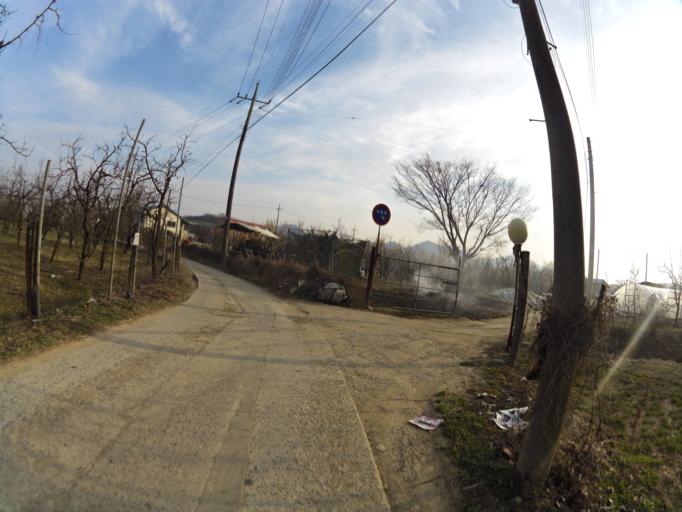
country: KR
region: Gyeongsangbuk-do
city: Gyeongsan-si
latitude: 35.8582
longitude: 128.7160
